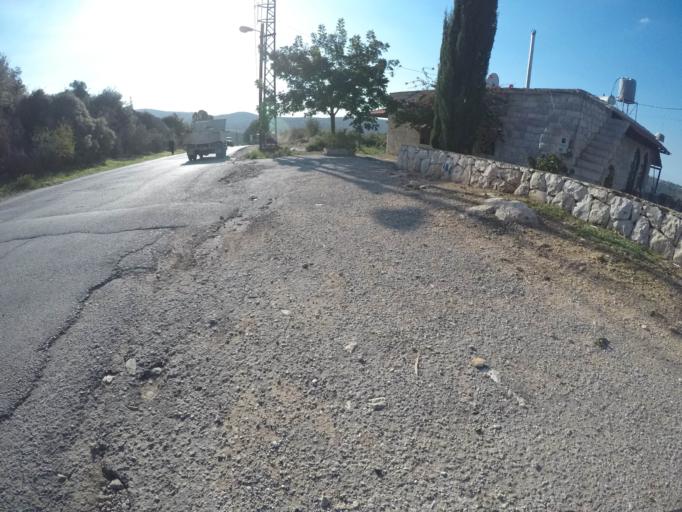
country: LB
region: Liban-Nord
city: Amioun
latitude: 34.2609
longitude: 35.8151
